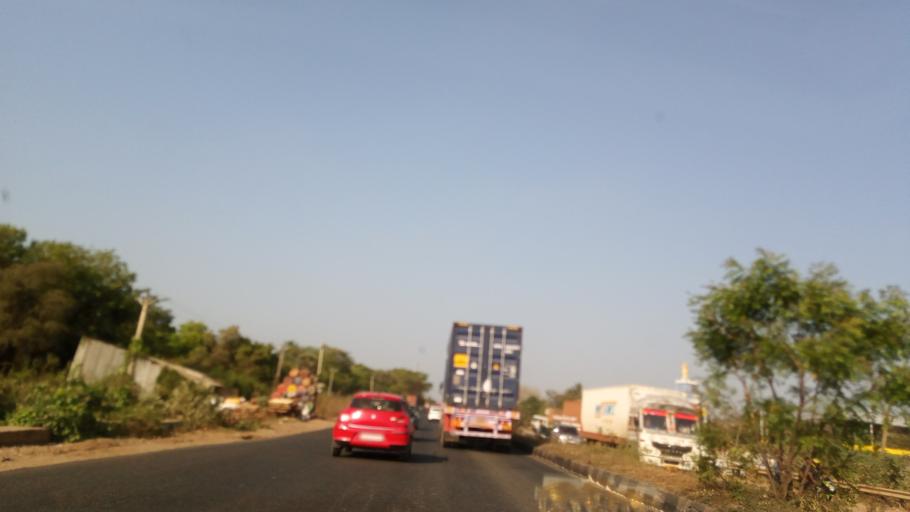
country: IN
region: Tamil Nadu
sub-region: Kancheepuram
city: Nandambakkam
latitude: 13.0257
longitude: 80.0256
